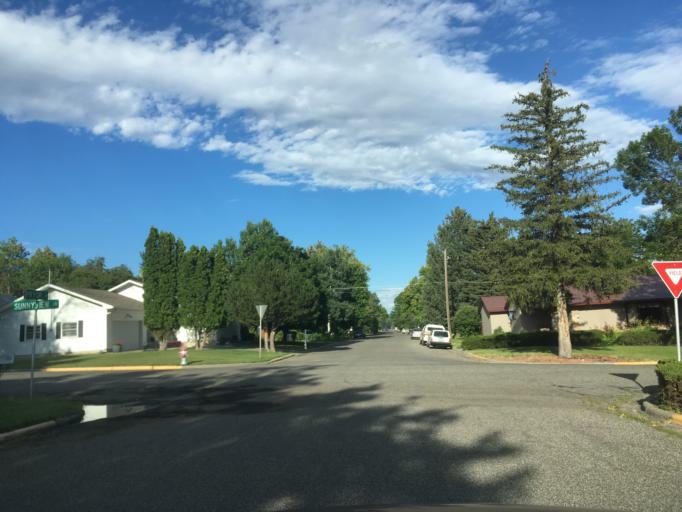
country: US
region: Montana
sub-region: Yellowstone County
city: Billings
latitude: 45.7969
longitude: -108.5732
